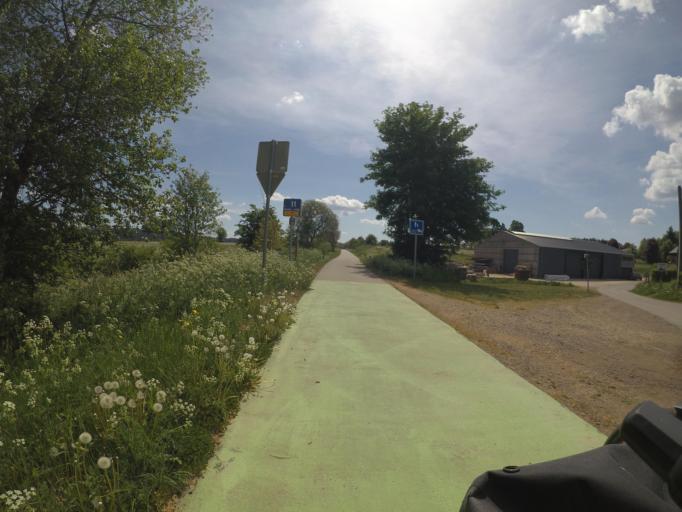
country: BE
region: Wallonia
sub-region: Province de Liege
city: Bullange
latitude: 50.3874
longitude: 6.2777
